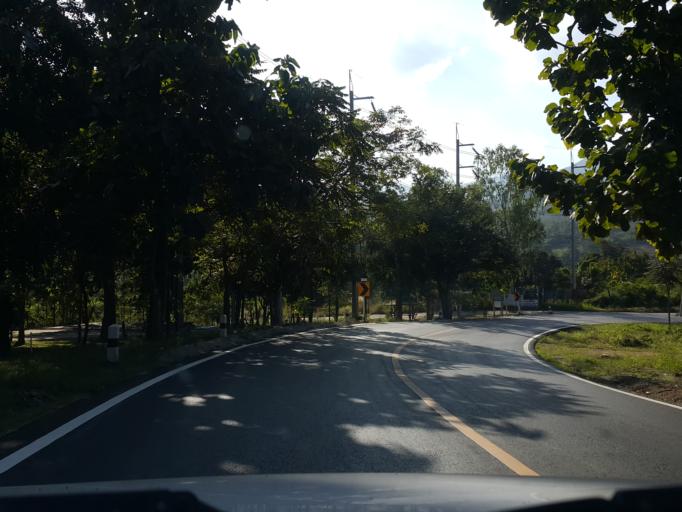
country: TH
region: Mae Hong Son
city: Mae Hi
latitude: 19.3129
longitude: 98.4429
